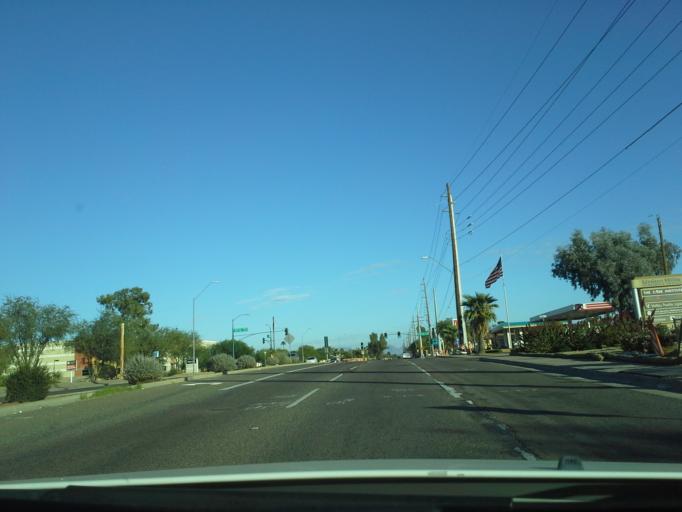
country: US
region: Arizona
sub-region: Maricopa County
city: Glendale
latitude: 33.6546
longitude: -112.1126
